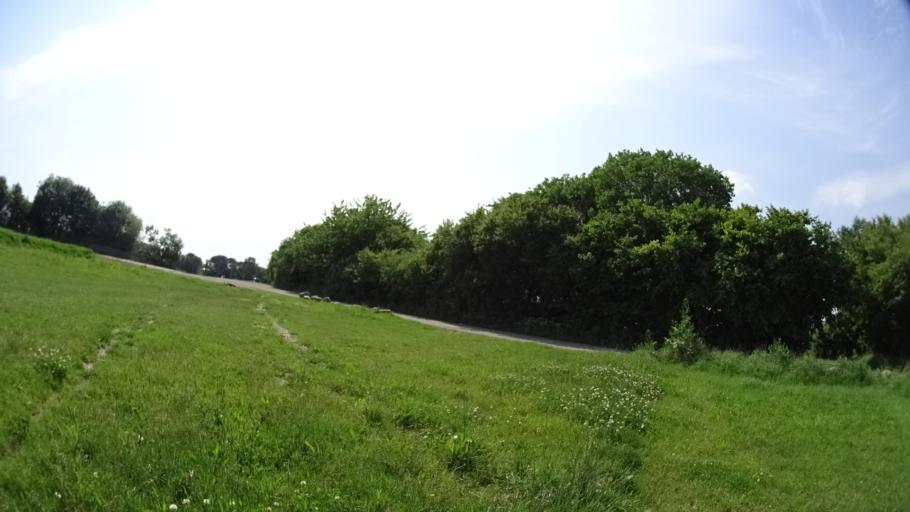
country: DK
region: Central Jutland
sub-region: Arhus Kommune
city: Arhus
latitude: 56.1485
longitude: 10.1713
